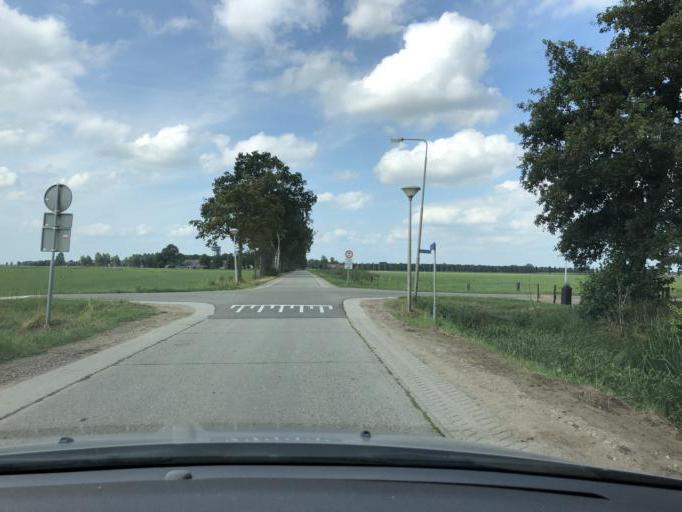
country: NL
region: Overijssel
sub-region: Gemeente Staphorst
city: Staphorst
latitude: 52.5729
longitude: 6.1973
